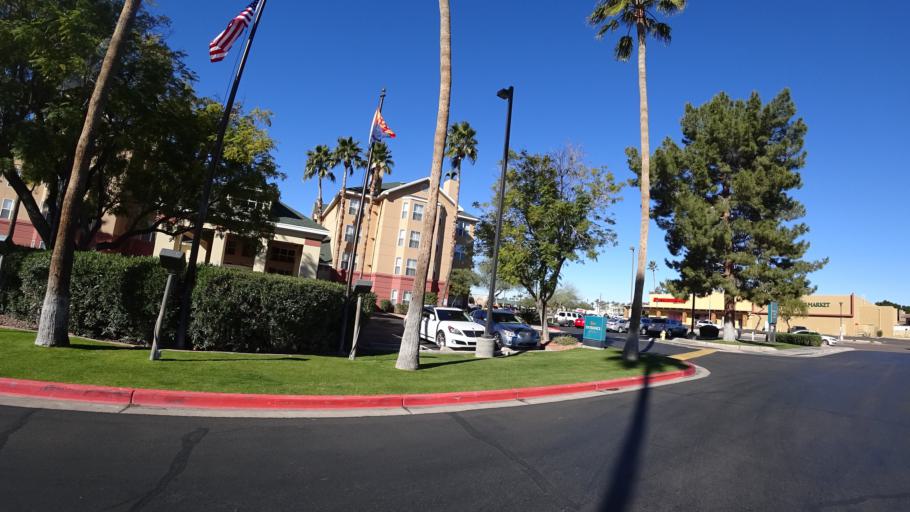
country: US
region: Arizona
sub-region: Maricopa County
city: Phoenix
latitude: 33.5051
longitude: -112.0373
